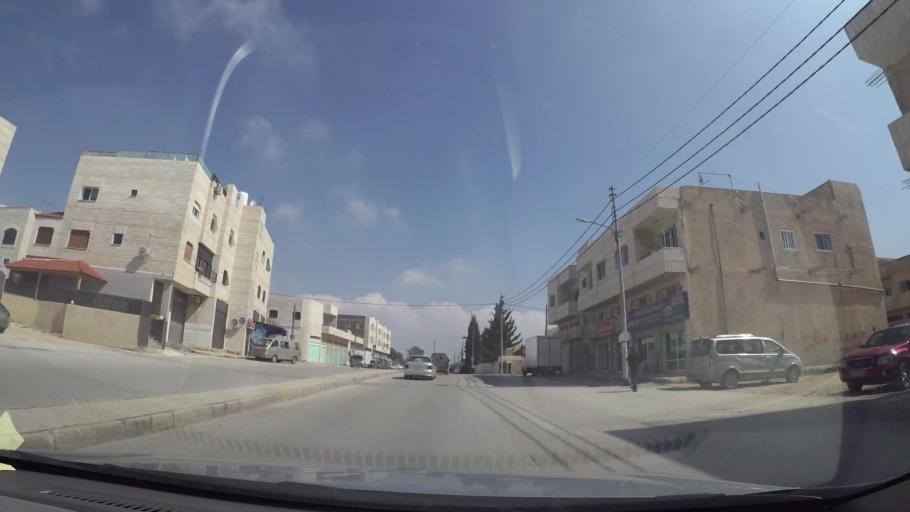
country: JO
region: Amman
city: Al Bunayyat ash Shamaliyah
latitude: 31.9034
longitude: 35.9030
